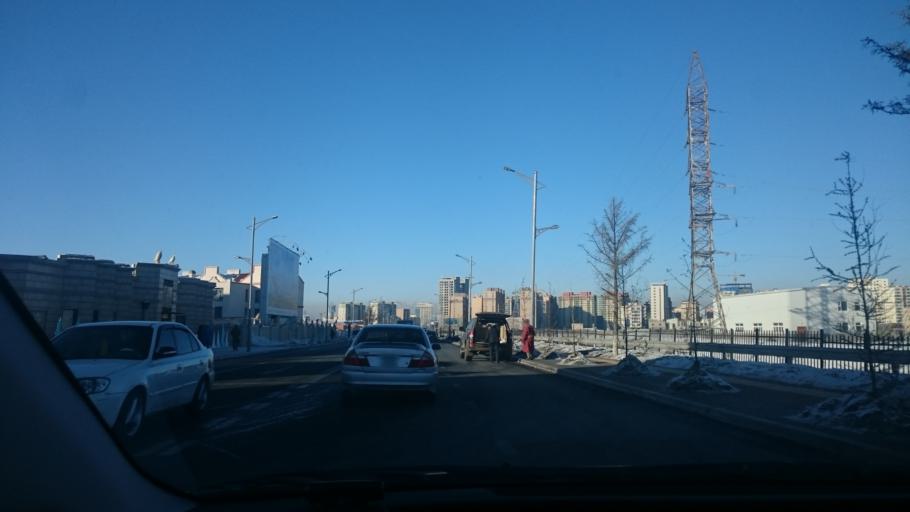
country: MN
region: Ulaanbaatar
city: Ulaanbaatar
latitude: 47.8946
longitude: 106.9353
